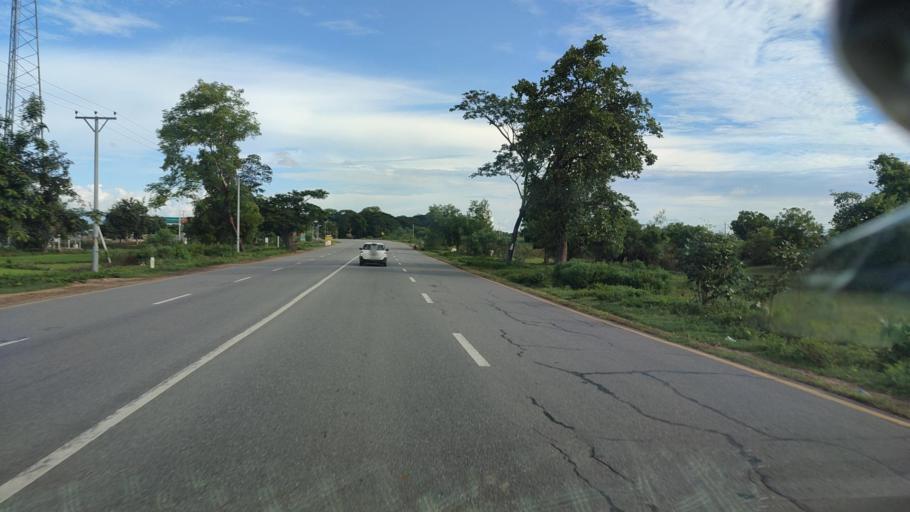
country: MM
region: Mandalay
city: Yamethin
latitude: 20.1953
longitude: 96.1833
